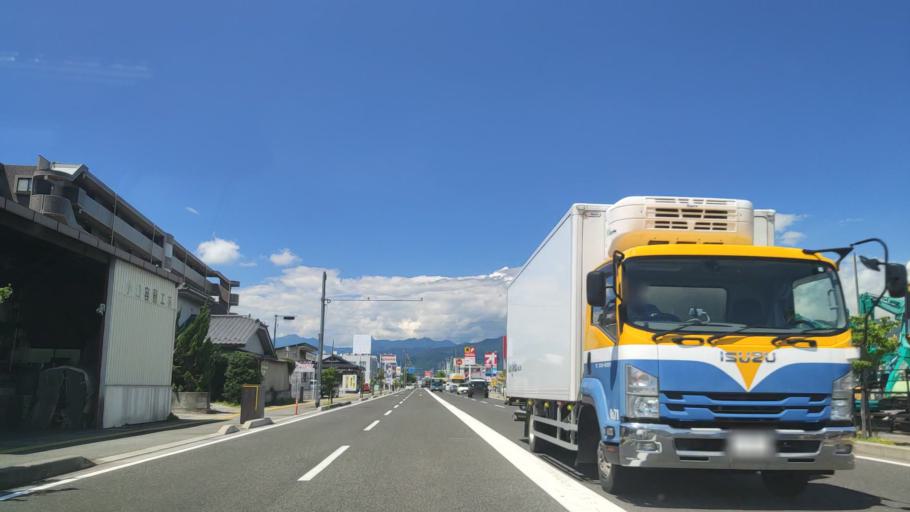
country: JP
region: Yamanashi
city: Kofu-shi
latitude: 35.6234
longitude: 138.5721
